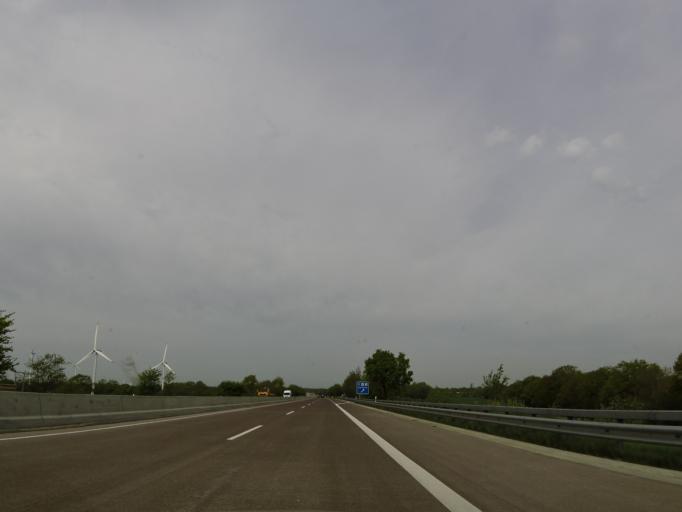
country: DE
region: Schleswig-Holstein
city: Horst
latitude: 53.8257
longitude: 9.6396
